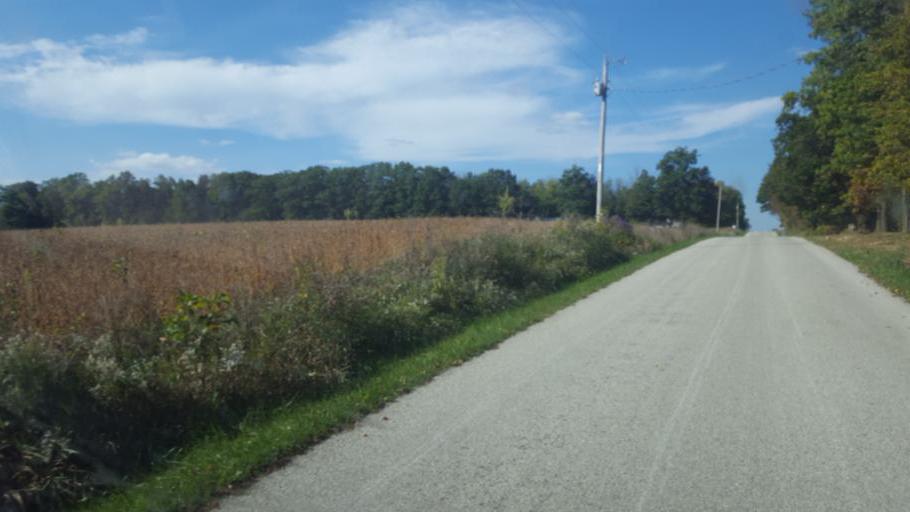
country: US
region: Ohio
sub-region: Morrow County
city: Mount Gilead
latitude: 40.5851
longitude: -82.7000
